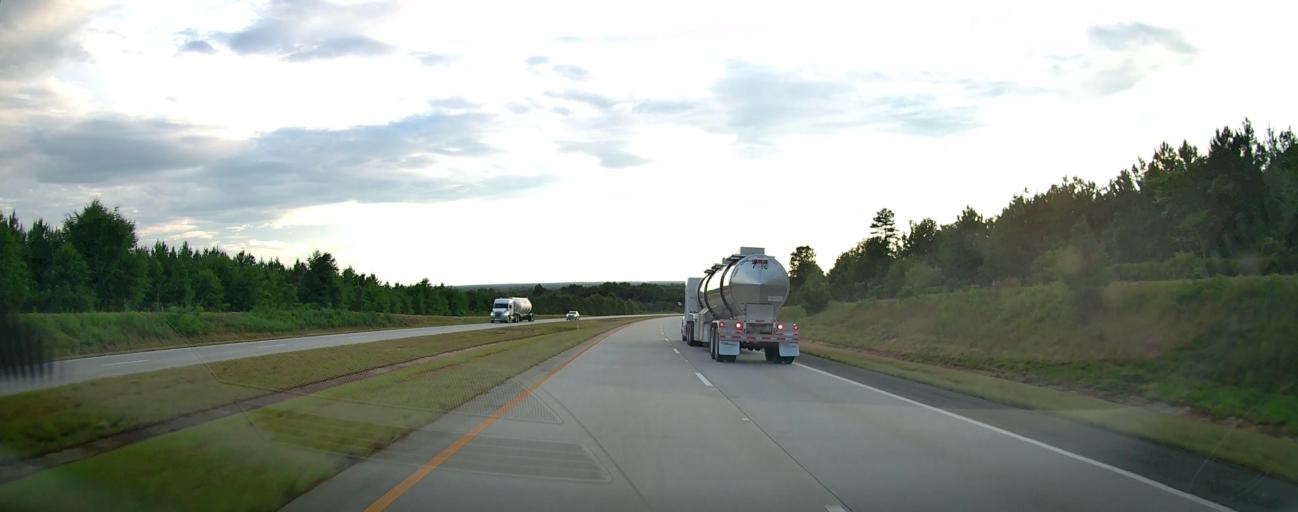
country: US
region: Georgia
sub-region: Macon County
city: Marshallville
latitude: 32.5462
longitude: -83.9913
